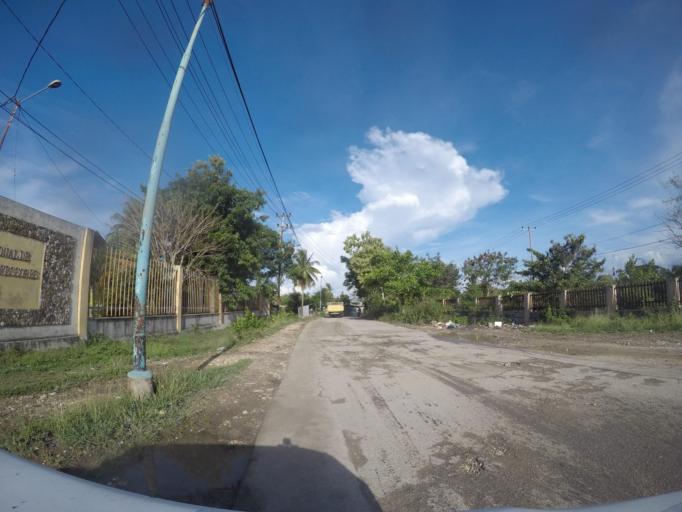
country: TL
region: Baucau
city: Baucau
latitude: -8.4839
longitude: 126.4554
